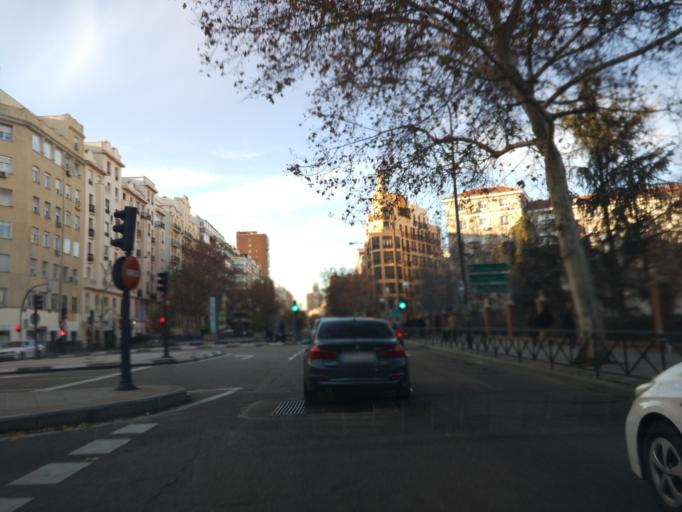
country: ES
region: Madrid
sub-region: Provincia de Madrid
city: Salamanca
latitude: 40.4297
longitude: -3.6700
